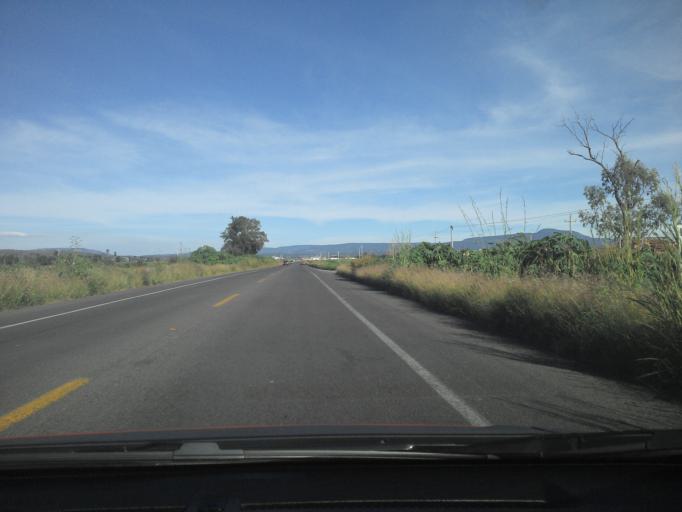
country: MX
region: Jalisco
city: El Refugio
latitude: 20.6656
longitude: -103.7702
